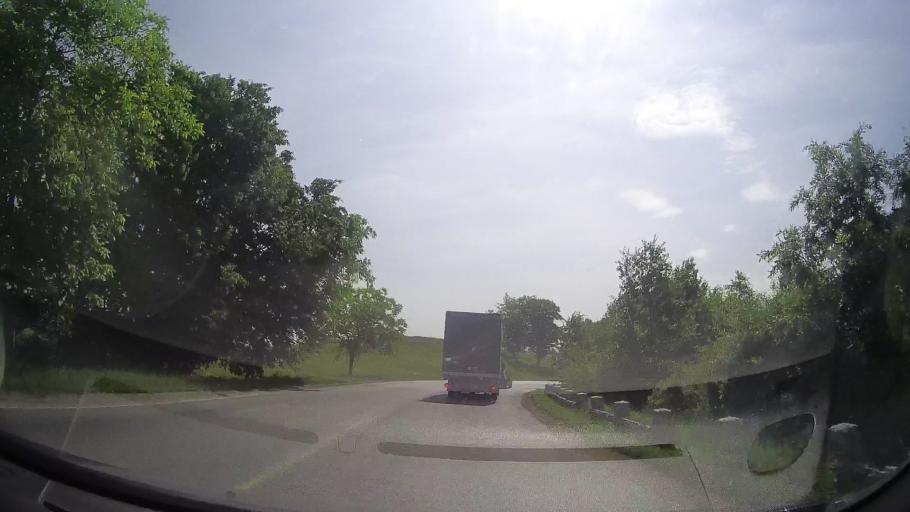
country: RO
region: Timis
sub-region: Comuna Pietroasa
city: Pietroasa
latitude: 45.8865
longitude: 22.4114
